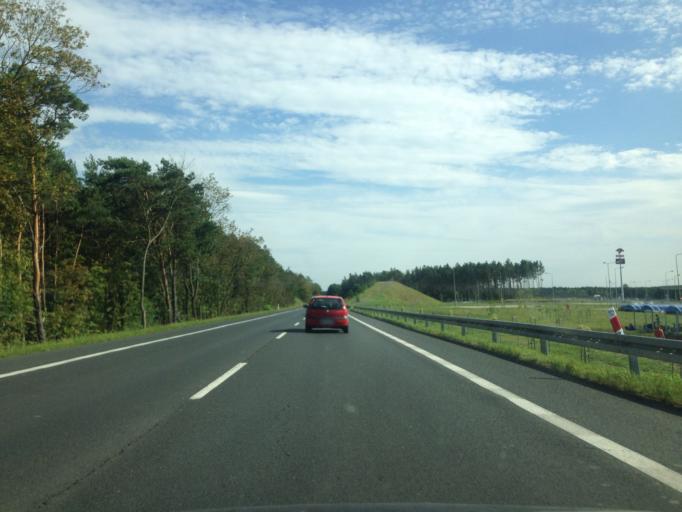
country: PL
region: Kujawsko-Pomorskie
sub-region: Powiat aleksandrowski
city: Aleksandrow Kujawski
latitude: 52.9017
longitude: 18.7248
